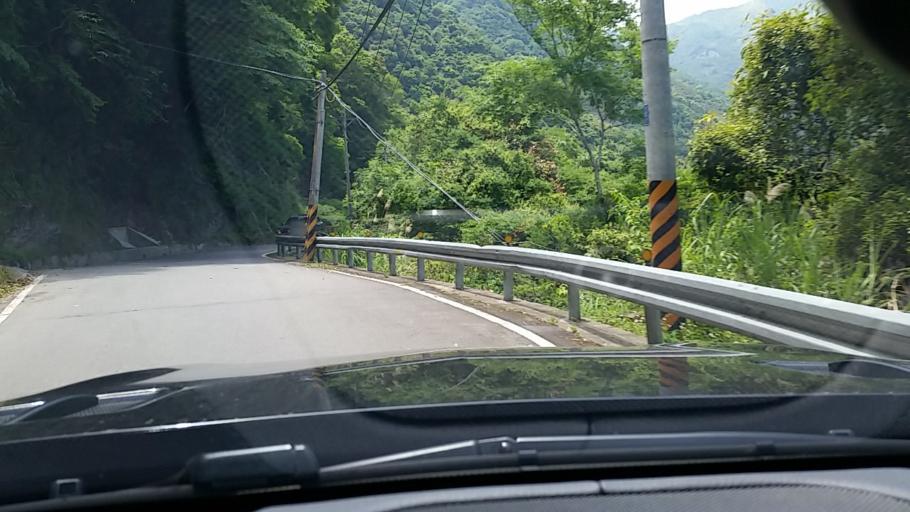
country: TW
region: Taiwan
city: Daxi
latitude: 24.6987
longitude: 121.3700
